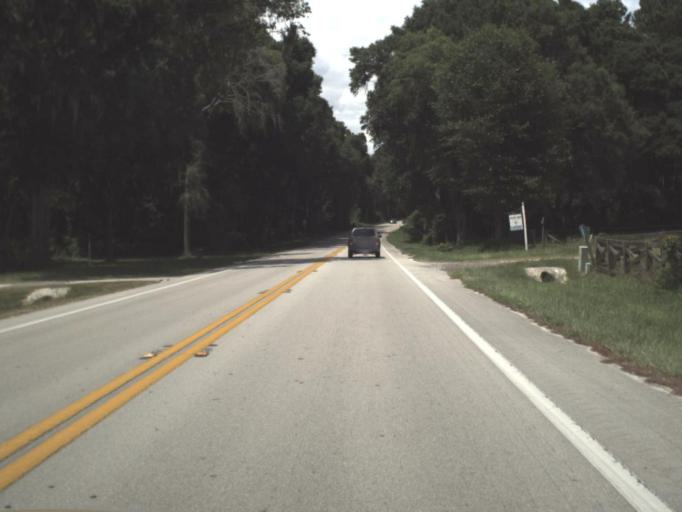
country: US
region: Florida
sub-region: Alachua County
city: High Springs
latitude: 29.8101
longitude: -82.6064
